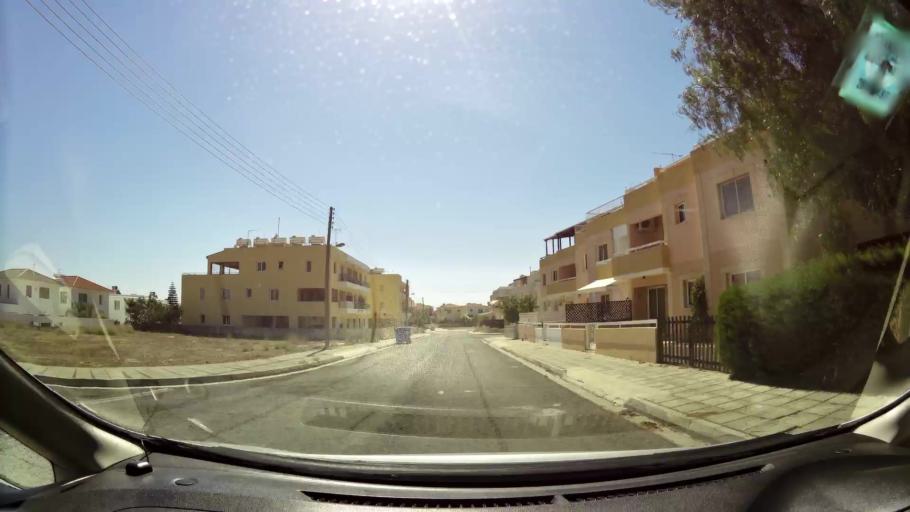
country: CY
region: Larnaka
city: Livadia
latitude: 34.9635
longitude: 33.6396
